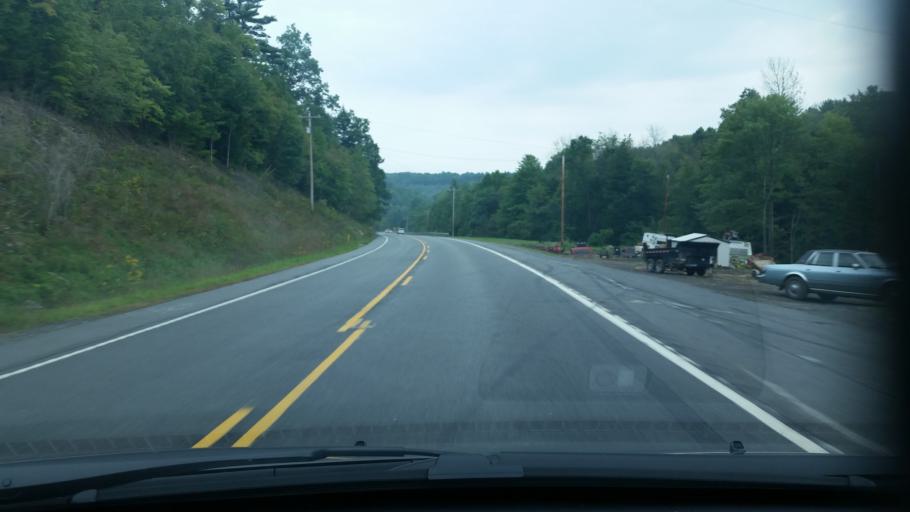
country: US
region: Pennsylvania
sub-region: Clearfield County
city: Shiloh
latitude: 41.0934
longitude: -78.2462
